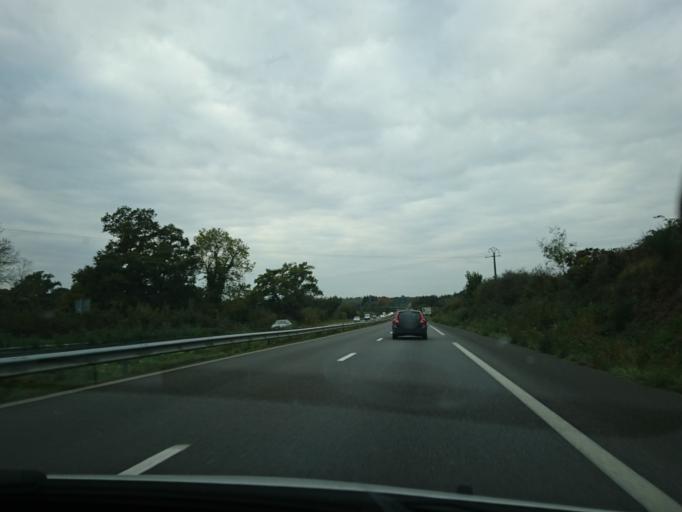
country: FR
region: Pays de la Loire
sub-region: Departement de la Loire-Atlantique
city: Pontchateau
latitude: 47.4336
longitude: -2.0675
